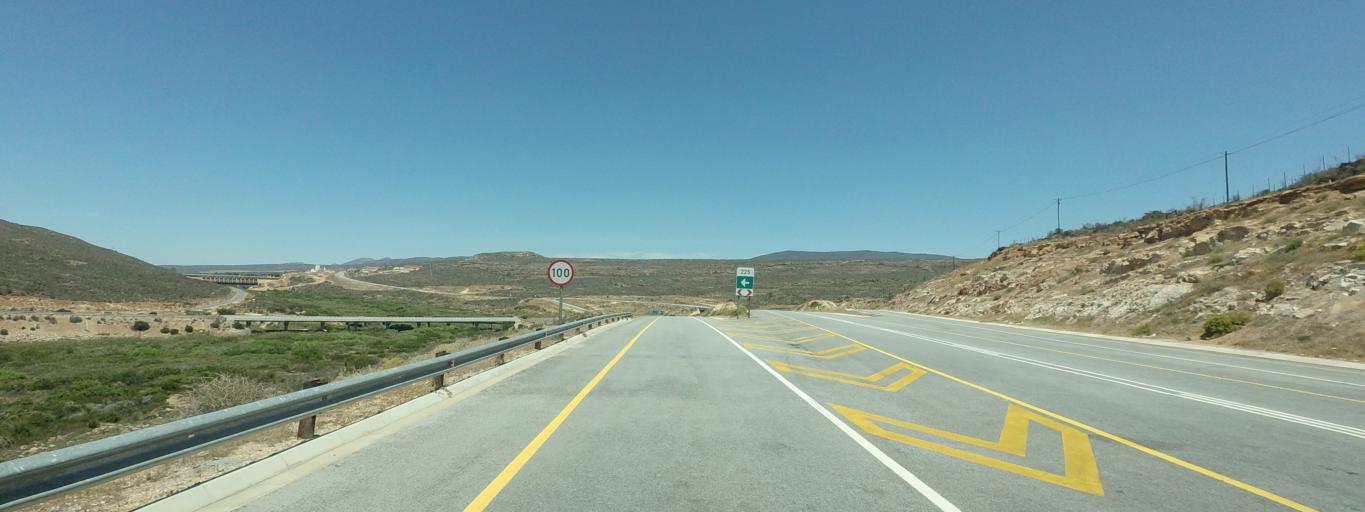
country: ZA
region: Western Cape
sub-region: West Coast District Municipality
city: Clanwilliam
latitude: -32.1695
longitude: 18.8698
